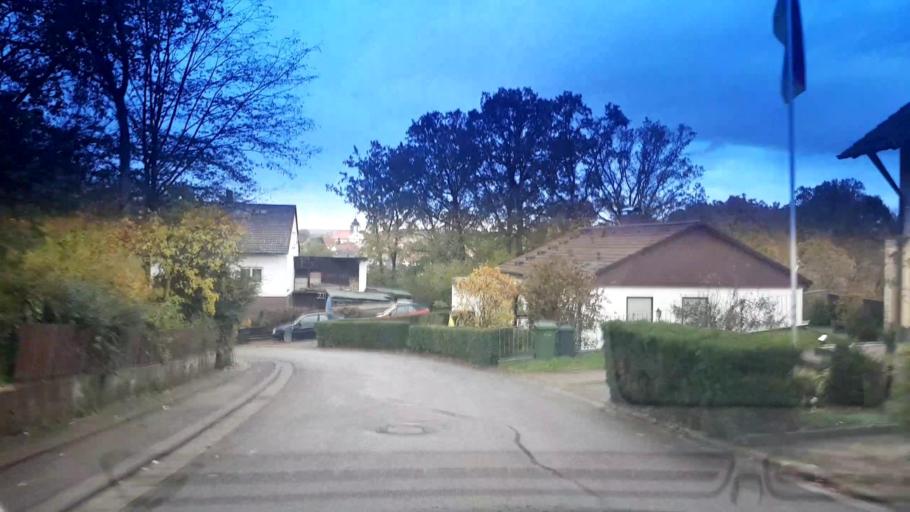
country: DE
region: Bavaria
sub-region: Upper Franconia
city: Viereth-Trunstadt
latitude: 49.9188
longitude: 10.7766
